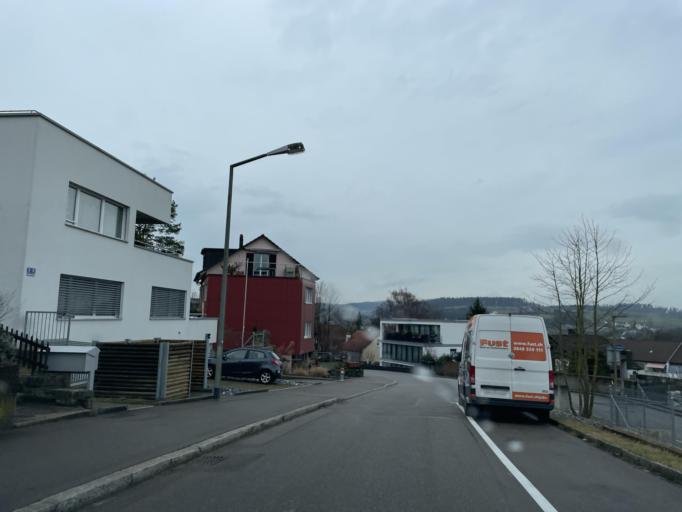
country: CH
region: Zurich
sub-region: Bezirk Winterthur
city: Wuelflingen (Kreis 6) / Lindenplatz
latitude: 47.5060
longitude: 8.6954
